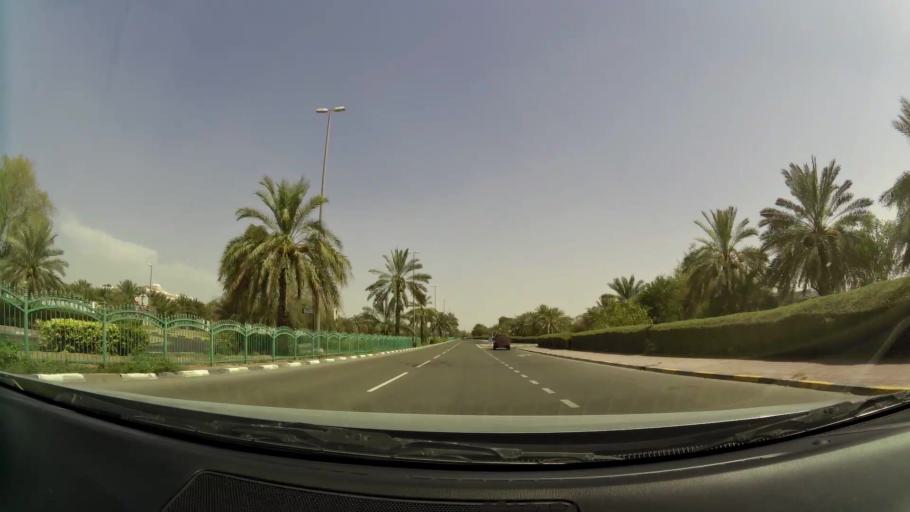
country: AE
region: Abu Dhabi
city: Al Ain
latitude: 24.2382
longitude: 55.7039
